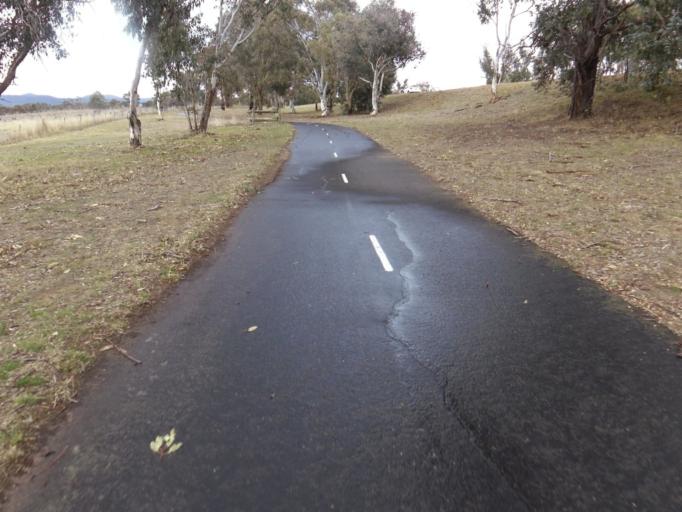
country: AU
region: Australian Capital Territory
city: Macquarie
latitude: -35.2728
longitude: 149.0760
